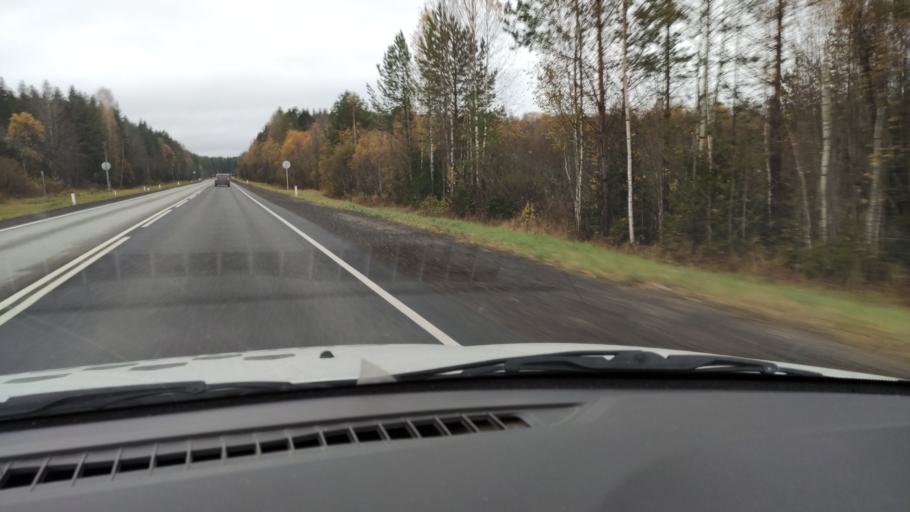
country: RU
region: Kirov
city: Belaya Kholunitsa
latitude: 58.8855
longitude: 50.8737
